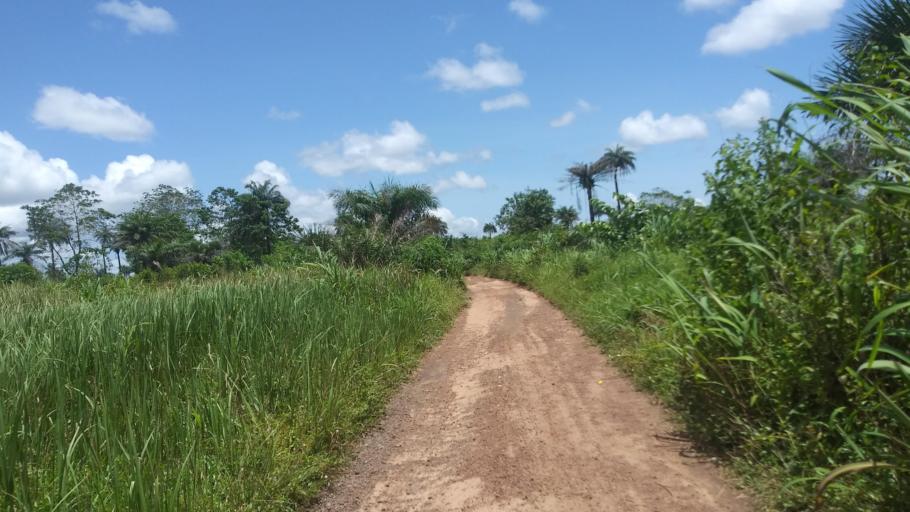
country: SL
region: Northern Province
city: Makeni
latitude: 8.8878
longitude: -12.0132
